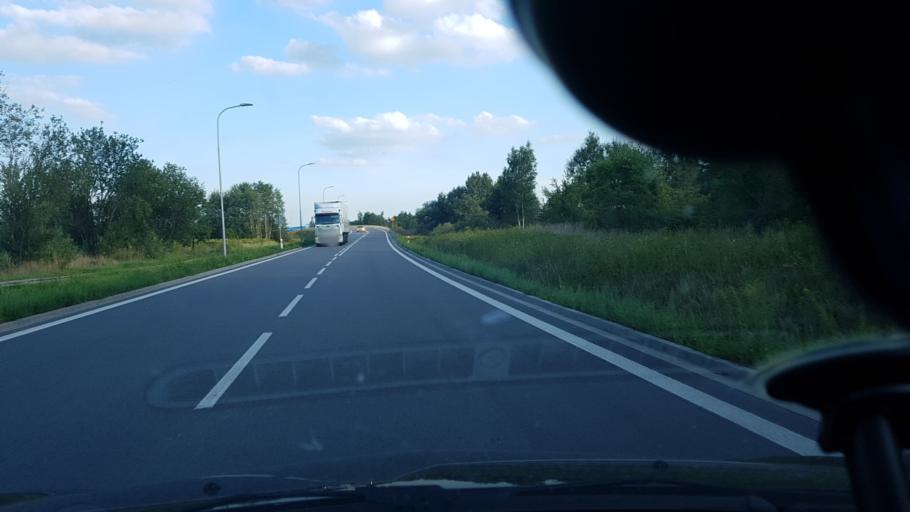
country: PL
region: Lesser Poland Voivodeship
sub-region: Powiat krakowski
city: Kryspinow
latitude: 50.0392
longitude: 19.8120
